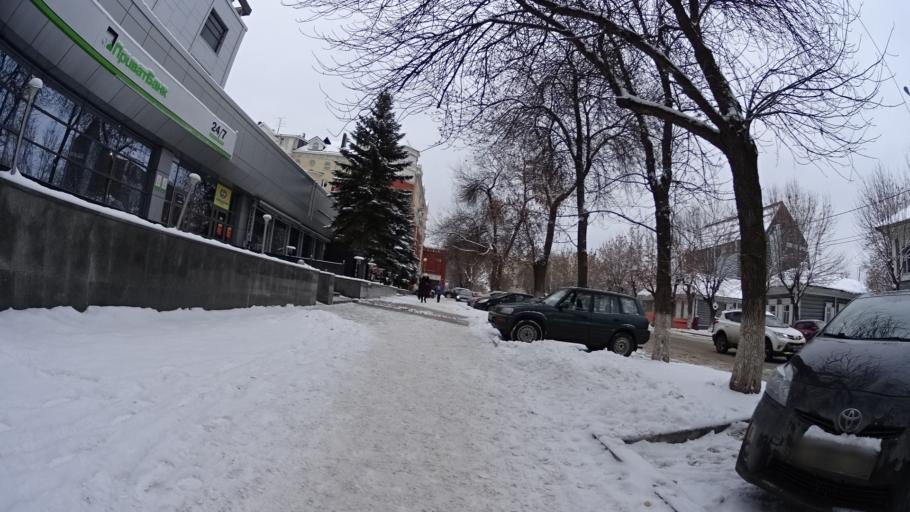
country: RU
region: Bashkortostan
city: Ufa
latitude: 54.7252
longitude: 55.9377
